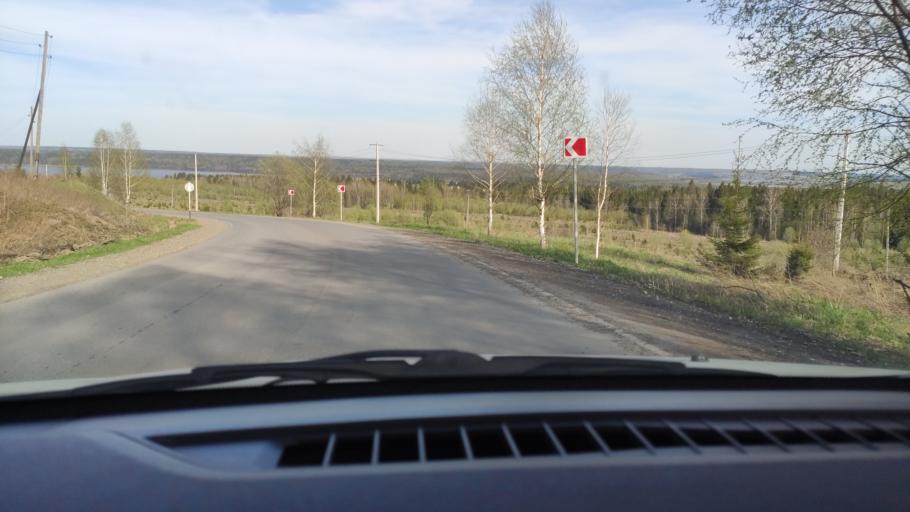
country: RU
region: Perm
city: Novyye Lyady
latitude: 57.9202
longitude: 56.6687
